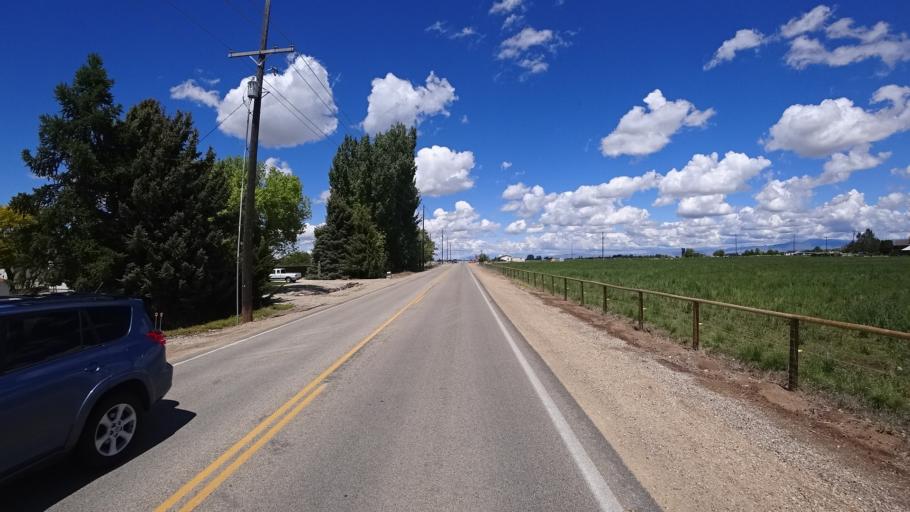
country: US
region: Idaho
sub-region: Ada County
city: Meridian
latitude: 43.5597
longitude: -116.4338
